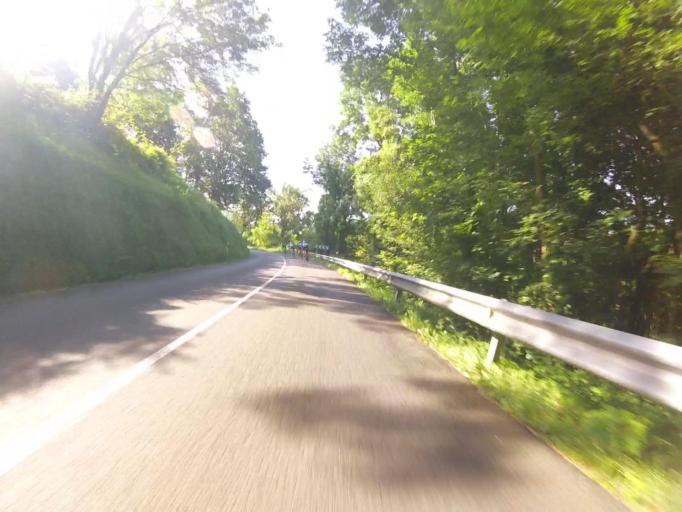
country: ES
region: Basque Country
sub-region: Provincia de Guipuzcoa
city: Asteasu
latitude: 43.2032
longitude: -2.1091
